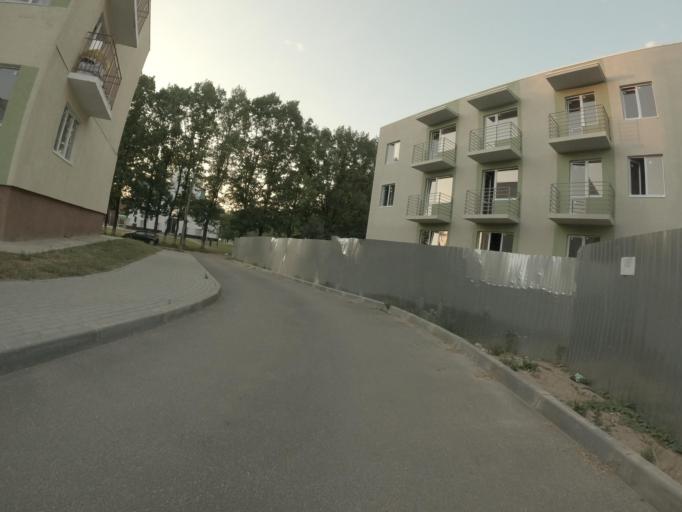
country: RU
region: Leningrad
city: Pavlovo
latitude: 59.8474
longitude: 30.9370
